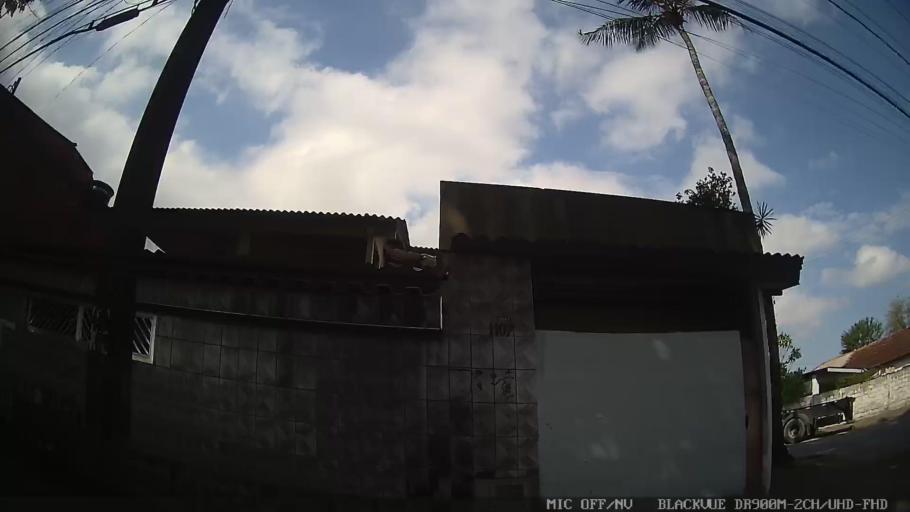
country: BR
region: Sao Paulo
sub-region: Santos
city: Santos
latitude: -23.9478
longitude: -46.3010
